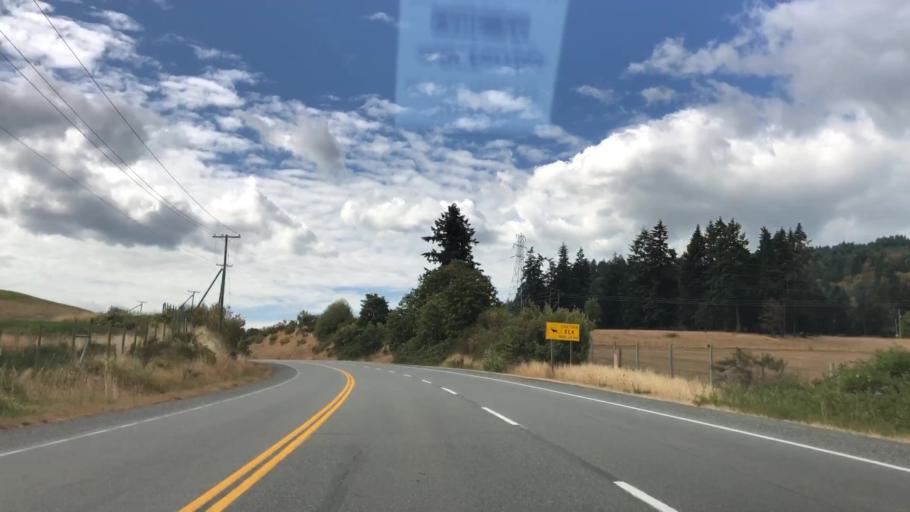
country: CA
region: British Columbia
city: Duncan
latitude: 48.8141
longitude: -123.7431
